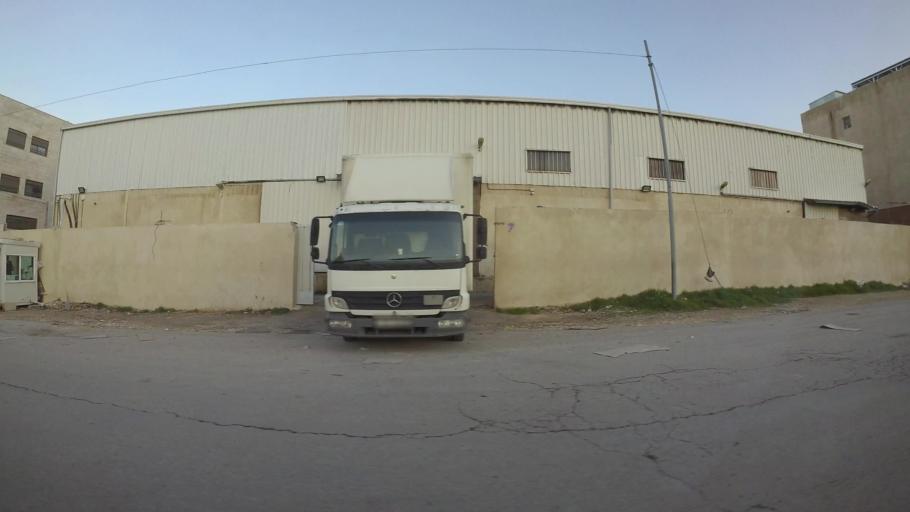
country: JO
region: Amman
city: Al Bunayyat ash Shamaliyah
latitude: 31.9093
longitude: 35.9187
